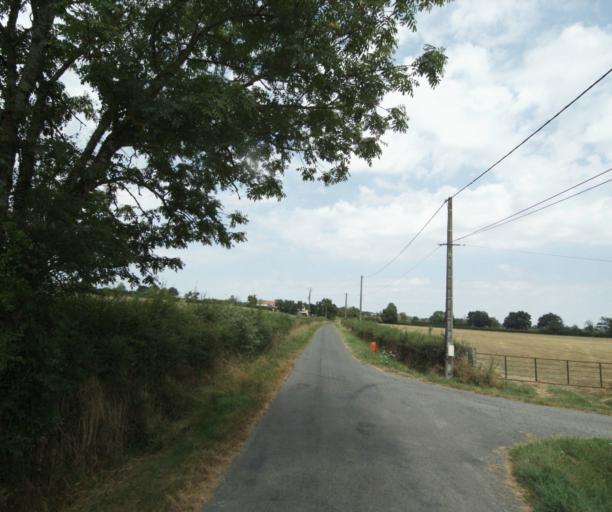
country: FR
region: Bourgogne
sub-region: Departement de Saone-et-Loire
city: Gueugnon
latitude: 46.5863
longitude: 4.0411
